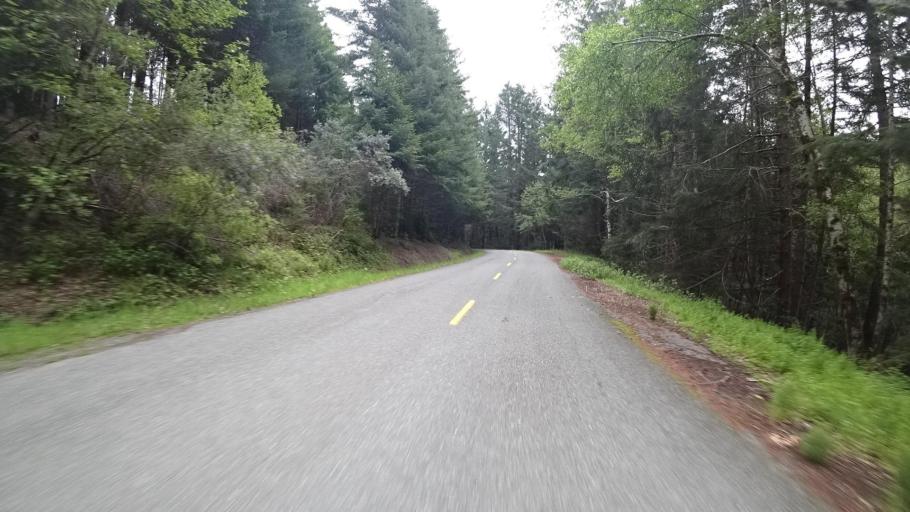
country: US
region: California
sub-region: Humboldt County
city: Blue Lake
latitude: 40.9383
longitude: -123.8452
